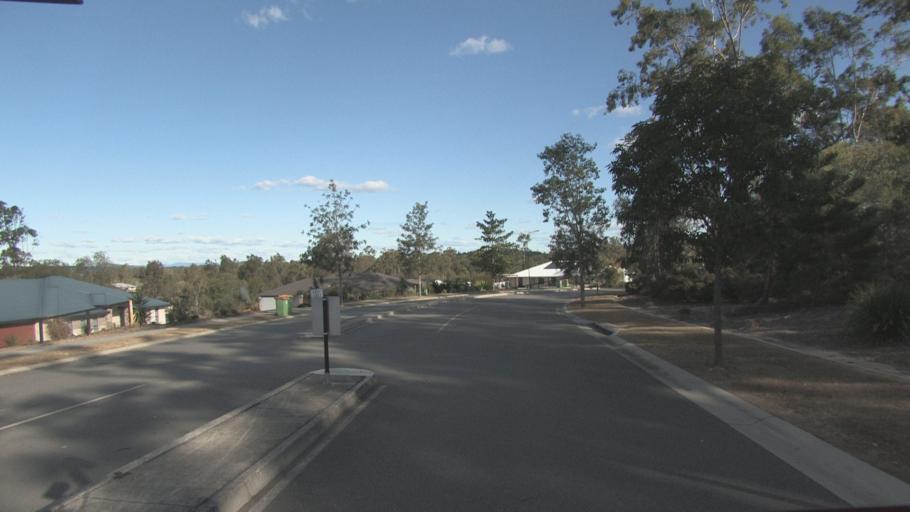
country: AU
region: Queensland
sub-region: Logan
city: North Maclean
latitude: -27.8241
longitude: 152.9800
